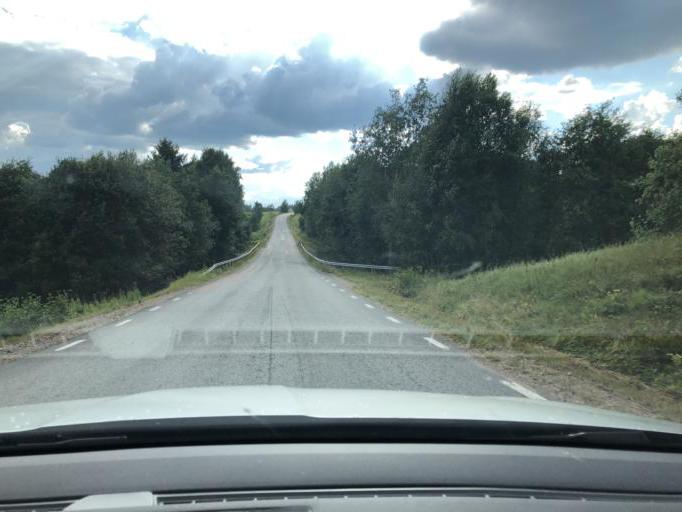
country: SE
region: Vaesternorrland
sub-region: Solleftea Kommun
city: Solleftea
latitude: 63.2038
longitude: 17.1250
